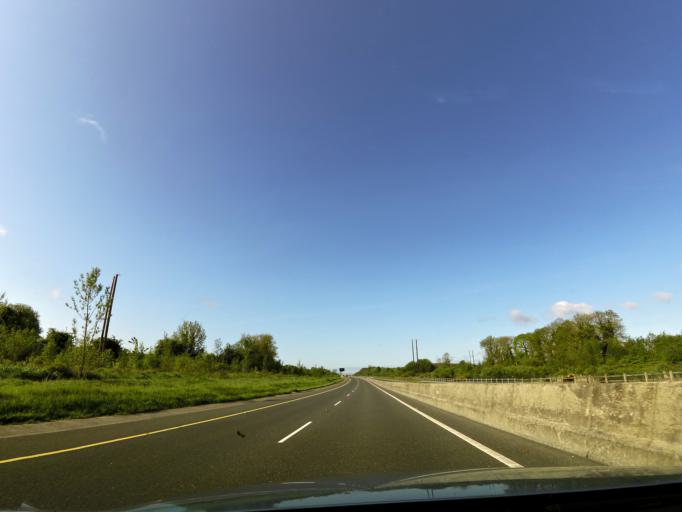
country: IE
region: Munster
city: Ballina
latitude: 52.7797
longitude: -8.3747
